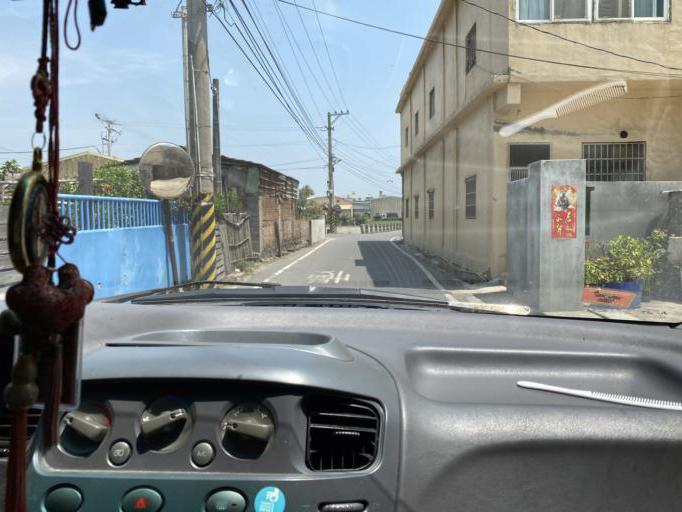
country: TW
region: Taiwan
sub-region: Changhua
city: Chang-hua
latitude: 24.0322
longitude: 120.4072
